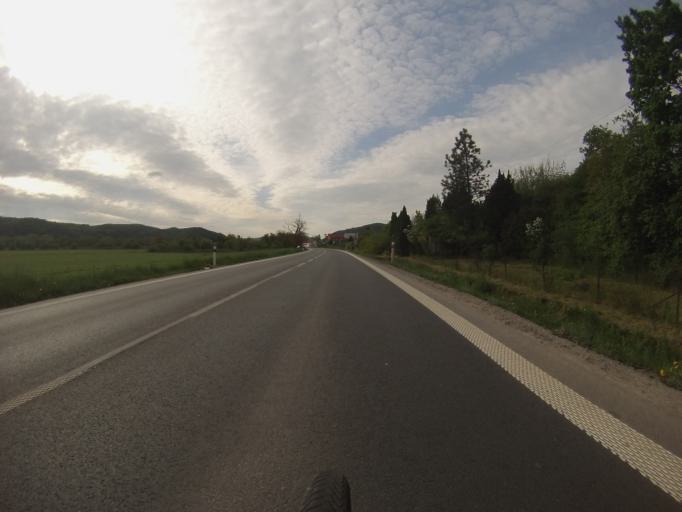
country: CZ
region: South Moravian
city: Tisnov
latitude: 49.3344
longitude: 16.4370
